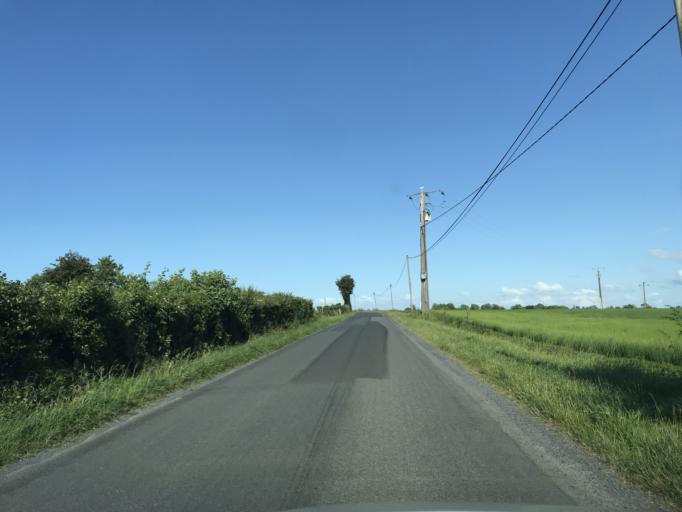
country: FR
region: Lower Normandy
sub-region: Departement du Calvados
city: Grandcamp-Maisy
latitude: 49.3806
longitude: -1.0706
